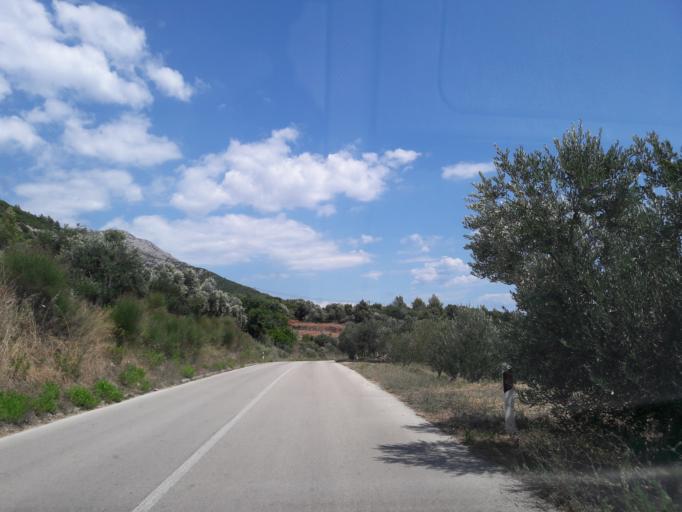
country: HR
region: Dubrovacko-Neretvanska
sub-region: Grad Korcula
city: Zrnovo
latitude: 42.9861
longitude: 17.0962
